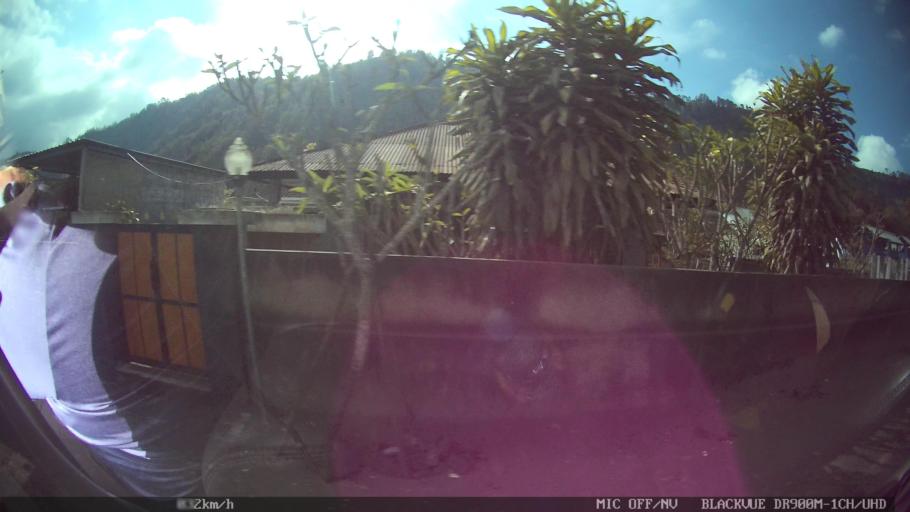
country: ID
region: Bali
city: Banjar Kedisan
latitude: -8.2194
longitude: 115.3638
